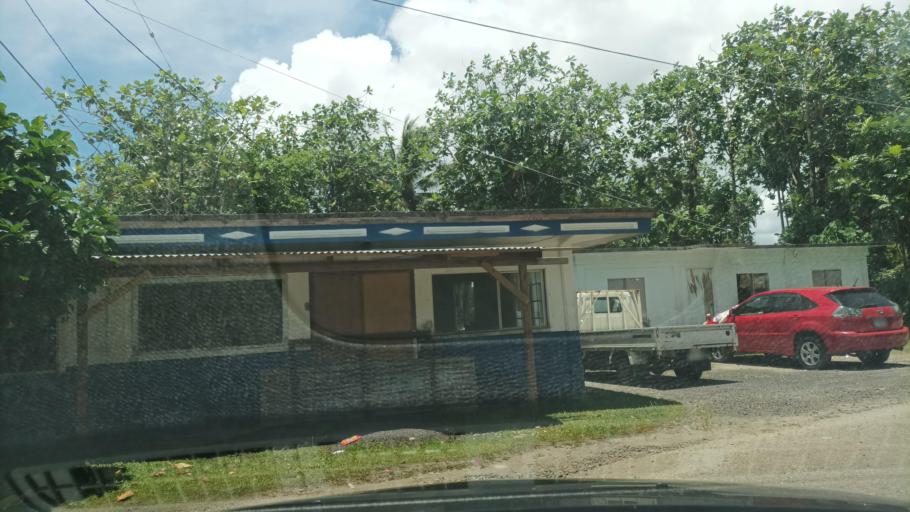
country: FM
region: Kosrae
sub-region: Lelu Municipality
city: Lelu
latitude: 5.3323
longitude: 163.0234
